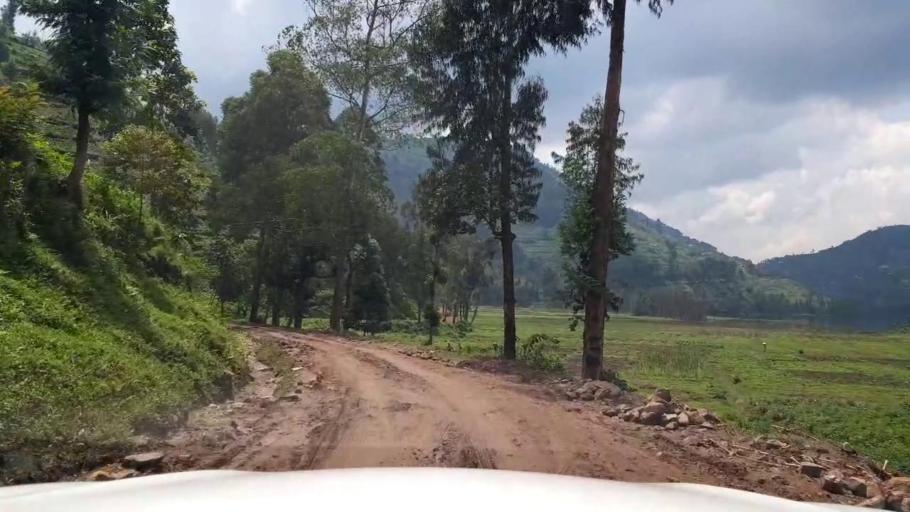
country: UG
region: Western Region
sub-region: Kisoro District
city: Kisoro
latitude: -1.3803
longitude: 29.7949
